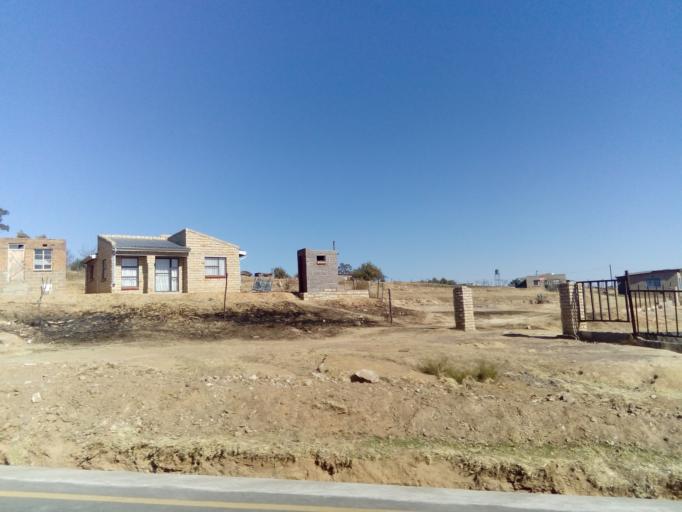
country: LS
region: Berea
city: Teyateyaneng
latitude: -29.1208
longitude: 27.8249
